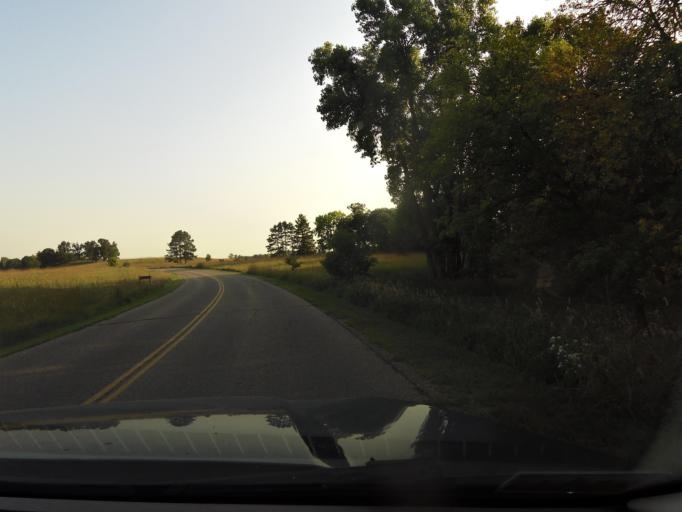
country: US
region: Minnesota
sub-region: Washington County
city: Afton
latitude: 44.8513
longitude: -92.7788
